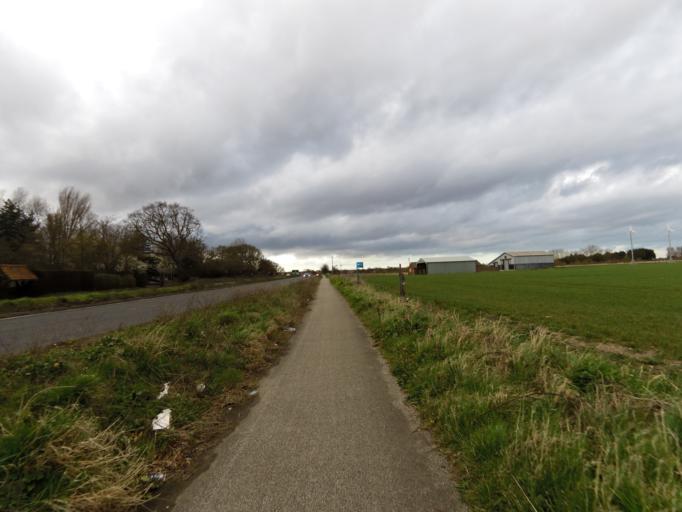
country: GB
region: England
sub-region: Norfolk
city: Hopton on Sea
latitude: 52.5513
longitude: 1.7184
